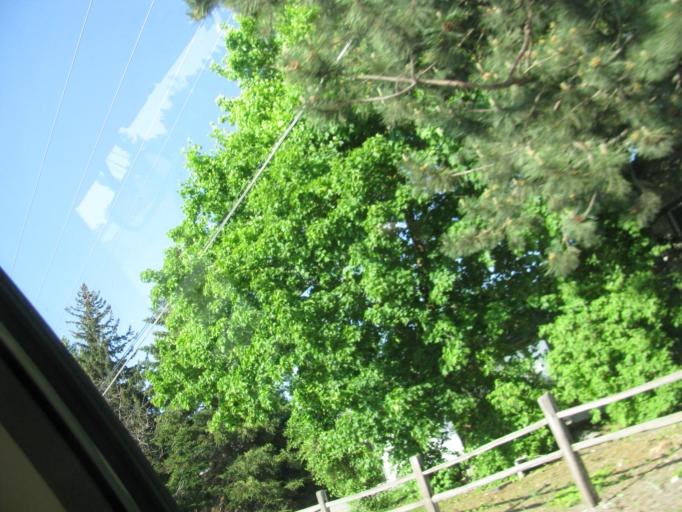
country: US
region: Washington
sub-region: Spokane County
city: Liberty Lake
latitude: 47.6541
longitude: -117.1536
